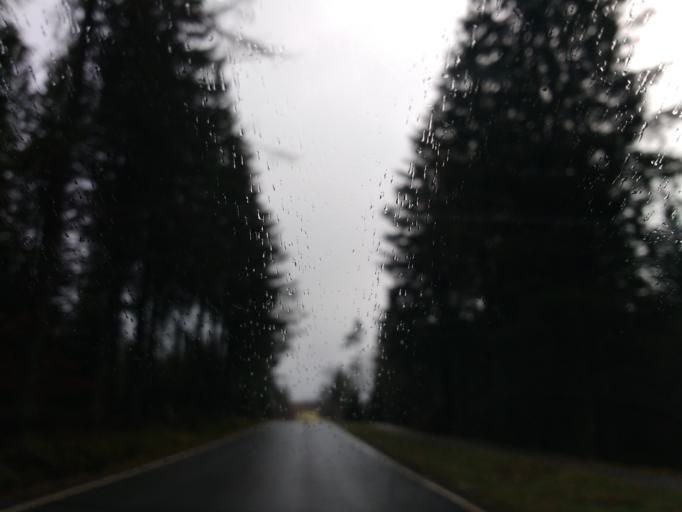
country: DE
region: Baden-Wuerttemberg
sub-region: Karlsruhe Region
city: Bad Rippoldsau-Schapbach
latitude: 48.4701
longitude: 8.2988
